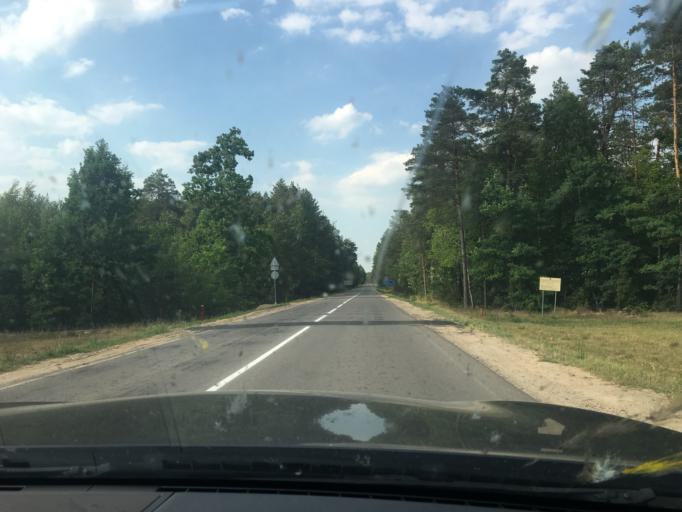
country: BY
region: Brest
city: Pruzhany
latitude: 52.7026
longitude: 24.3082
